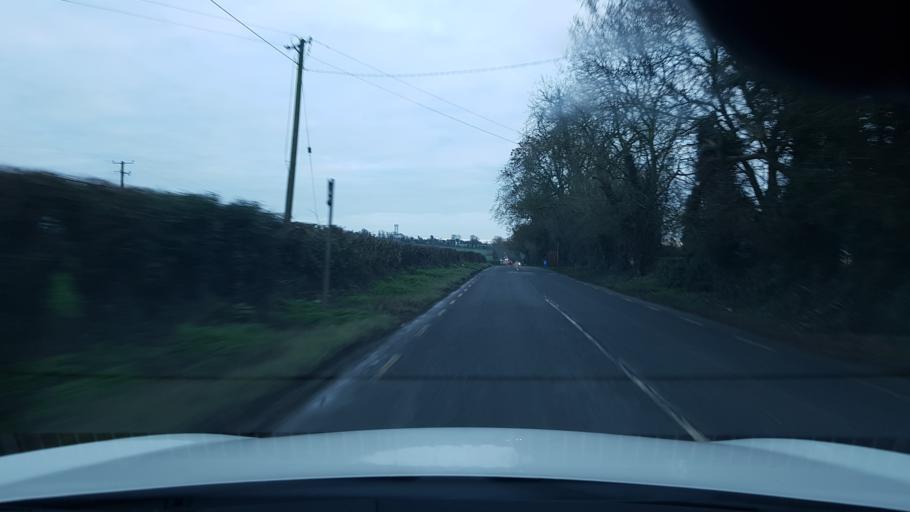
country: IE
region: Leinster
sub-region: An Mhi
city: Navan
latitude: 53.6976
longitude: -6.6780
